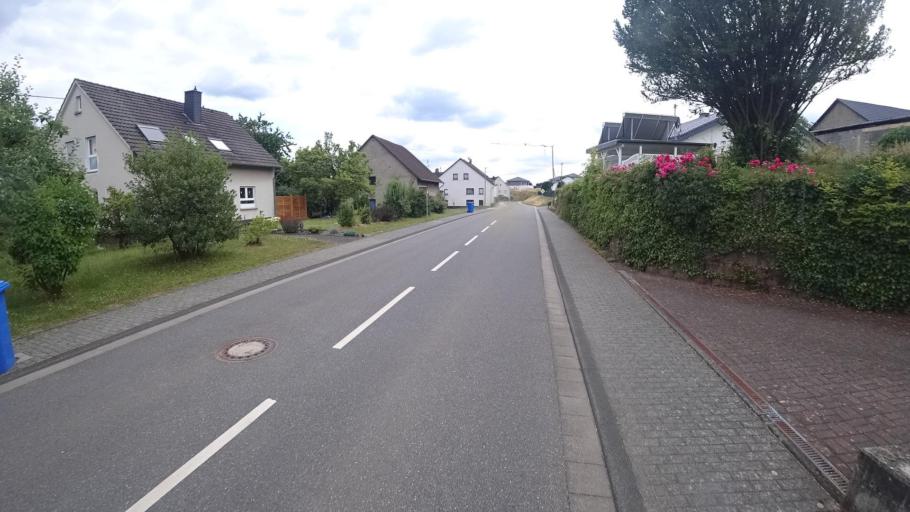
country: DE
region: Rheinland-Pfalz
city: Hemmelzen
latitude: 50.6951
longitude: 7.5815
